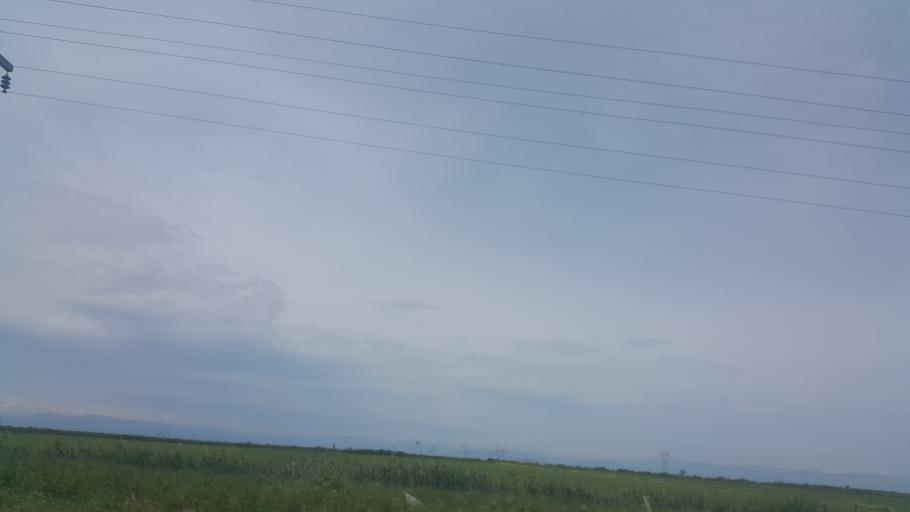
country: TR
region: Adana
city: Ceyhan
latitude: 37.0594
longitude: 35.9063
